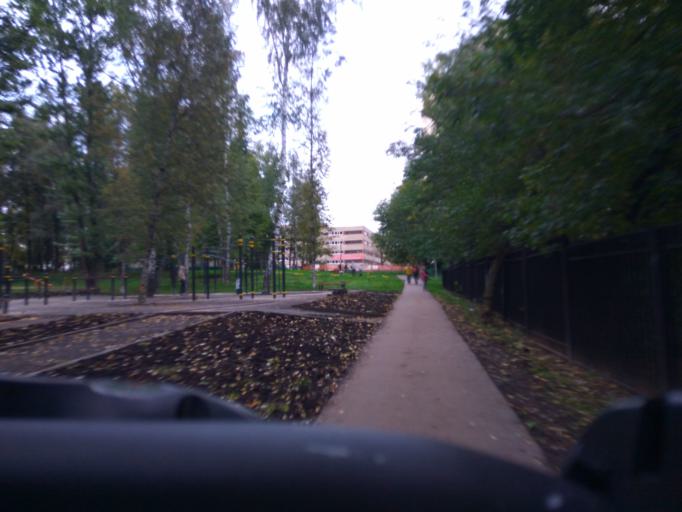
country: RU
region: Moskovskaya
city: Levoberezhnyy
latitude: 55.8613
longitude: 37.4790
